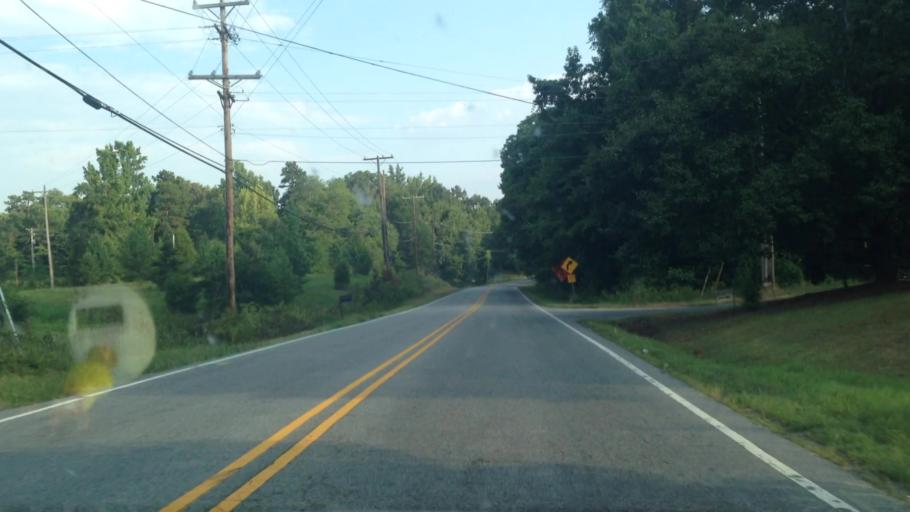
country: US
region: North Carolina
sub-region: Guilford County
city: High Point
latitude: 35.9944
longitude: -80.0625
